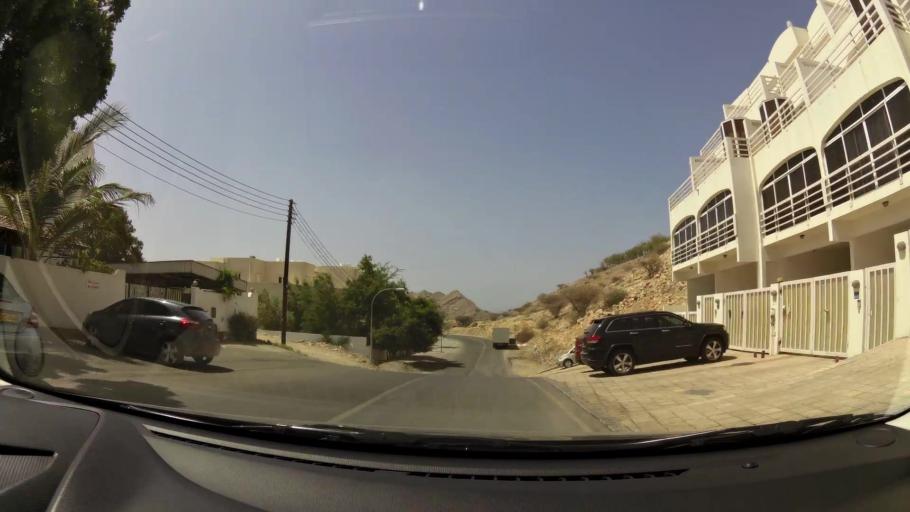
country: OM
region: Muhafazat Masqat
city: Muscat
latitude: 23.6196
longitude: 58.5089
